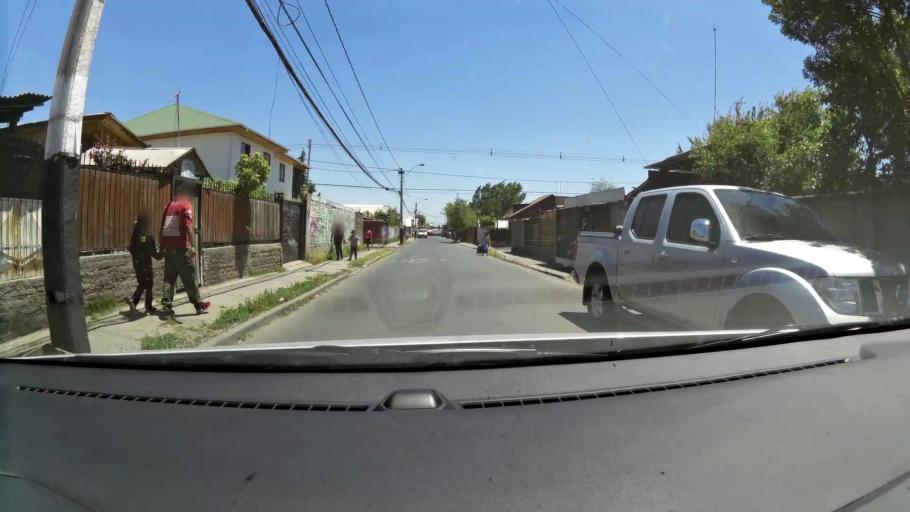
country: CL
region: Santiago Metropolitan
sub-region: Provincia de Maipo
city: San Bernardo
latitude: -33.5785
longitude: -70.6735
